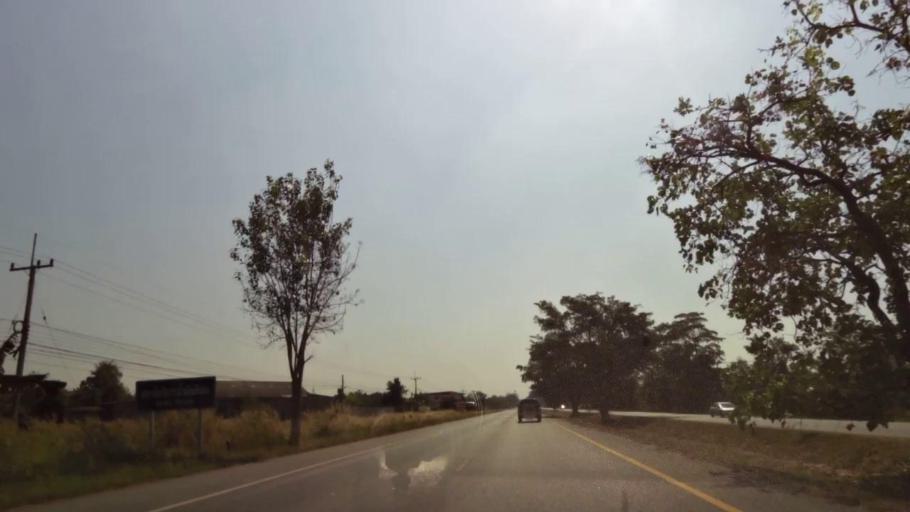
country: TH
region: Phichit
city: Bueng Na Rang
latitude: 16.3355
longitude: 100.1284
